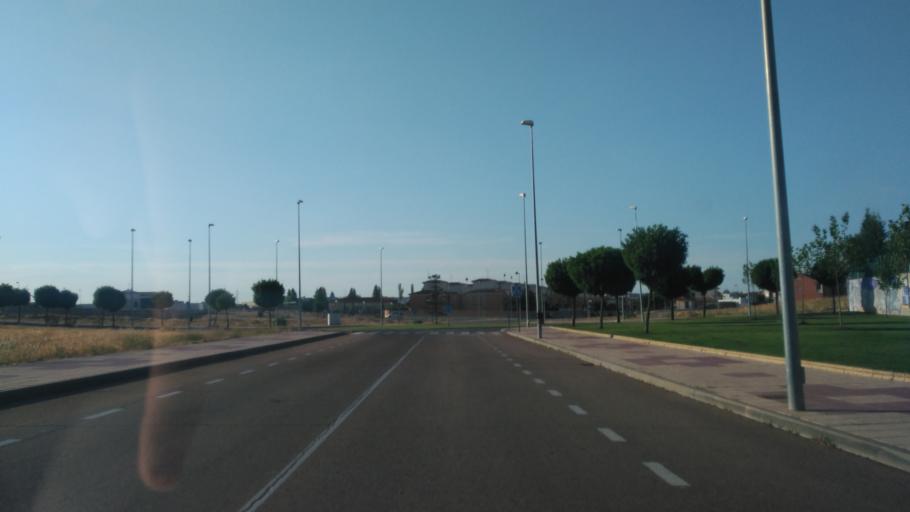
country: ES
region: Castille and Leon
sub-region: Provincia de Salamanca
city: Carbajosa de la Sagrada
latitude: 40.9370
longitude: -5.6443
